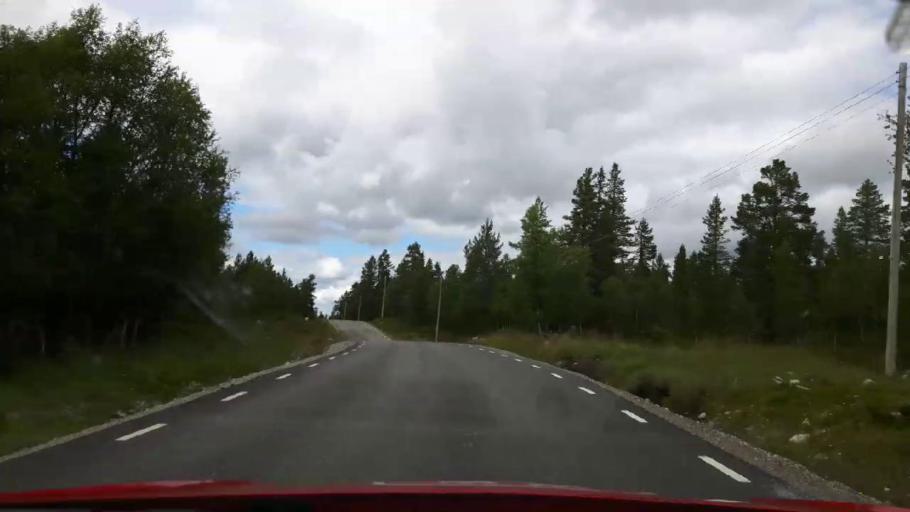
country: NO
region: Hedmark
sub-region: Engerdal
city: Engerdal
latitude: 62.3126
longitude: 12.8103
